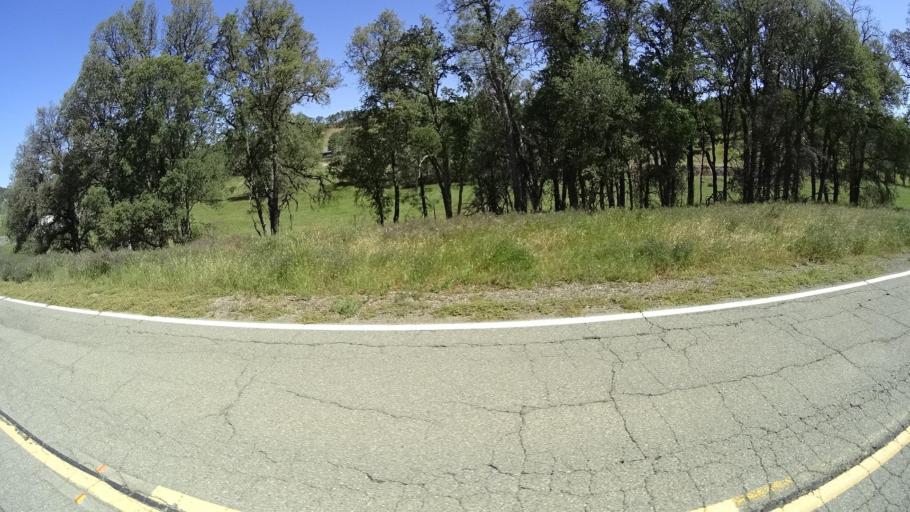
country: US
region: California
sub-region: Lake County
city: Hidden Valley Lake
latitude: 38.8854
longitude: -122.4726
